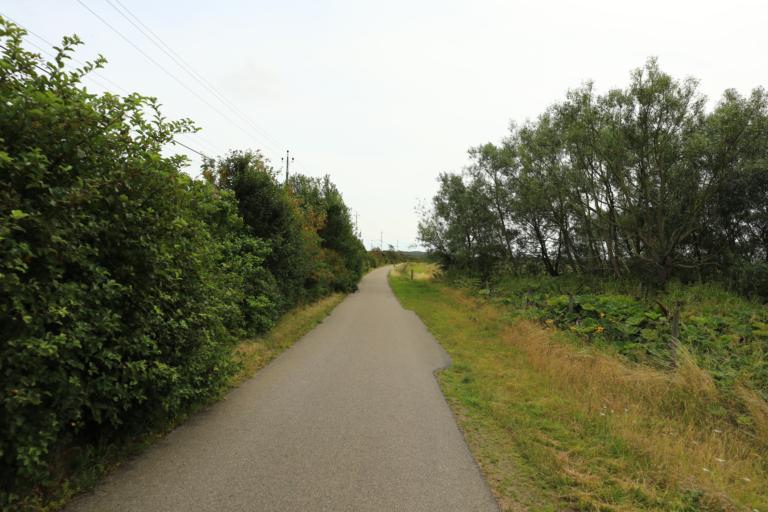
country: SE
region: Halland
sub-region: Varbergs Kommun
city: Varberg
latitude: 57.1401
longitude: 12.2585
